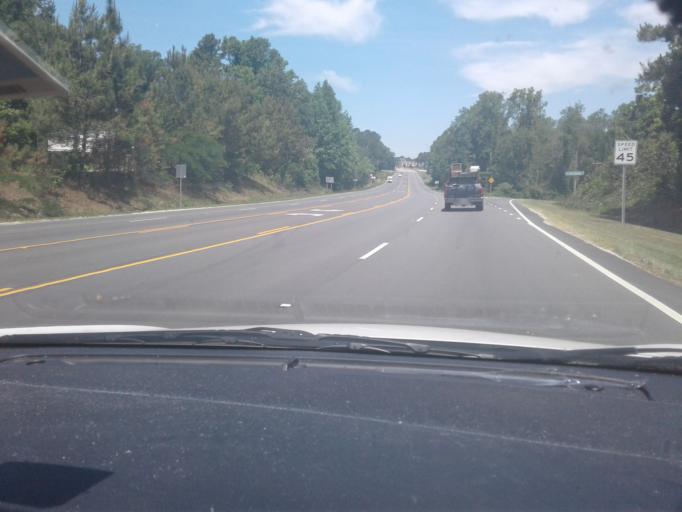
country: US
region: North Carolina
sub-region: Harnett County
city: Buies Creek
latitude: 35.3862
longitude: -78.7239
